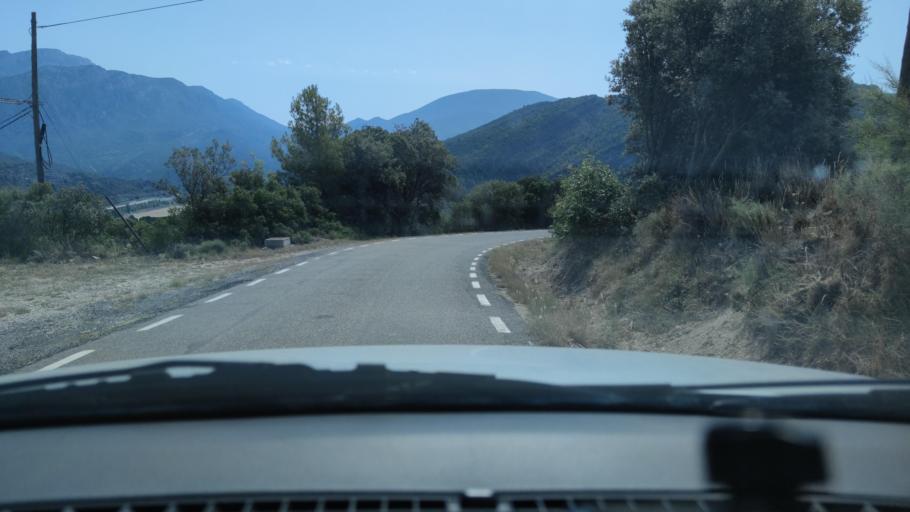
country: ES
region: Catalonia
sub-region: Provincia de Lleida
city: Ager
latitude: 42.0040
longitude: 0.8377
